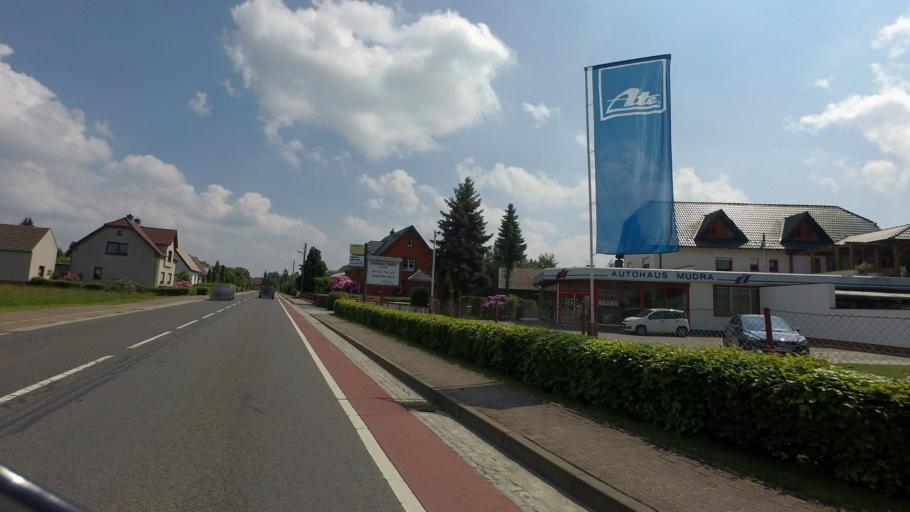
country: DE
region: Saxony
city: Schleife
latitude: 51.5463
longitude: 14.5327
